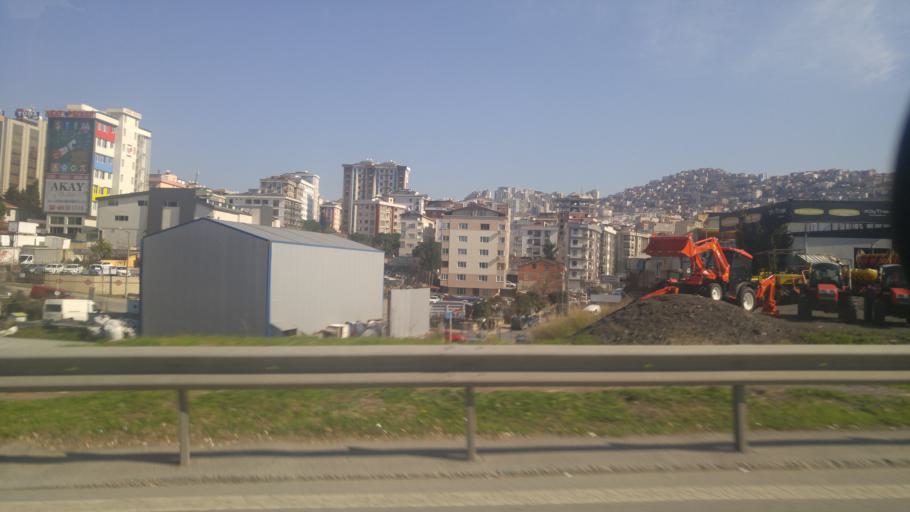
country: TR
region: Istanbul
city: Maltepe
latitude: 40.9338
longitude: 29.1416
